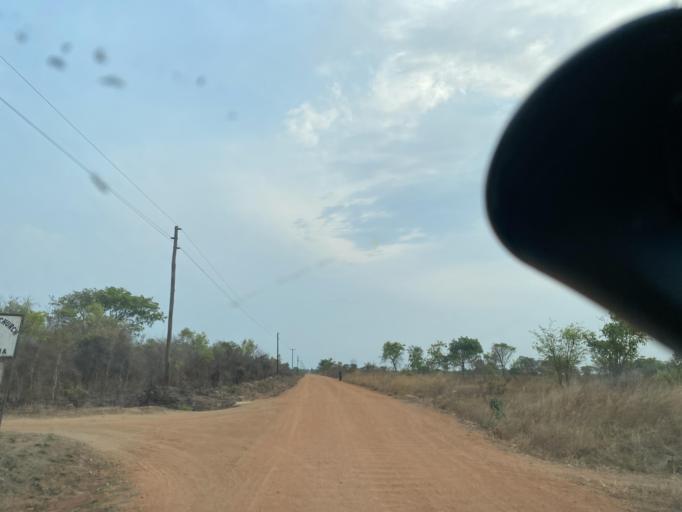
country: ZM
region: Lusaka
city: Chongwe
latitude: -15.2012
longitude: 28.5812
